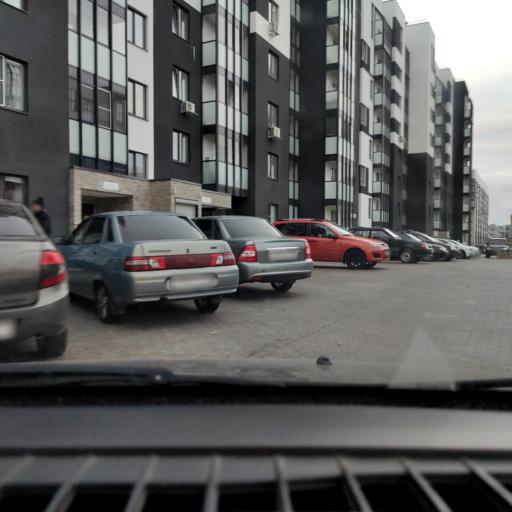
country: RU
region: Samara
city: Tol'yatti
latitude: 53.5266
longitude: 49.3411
